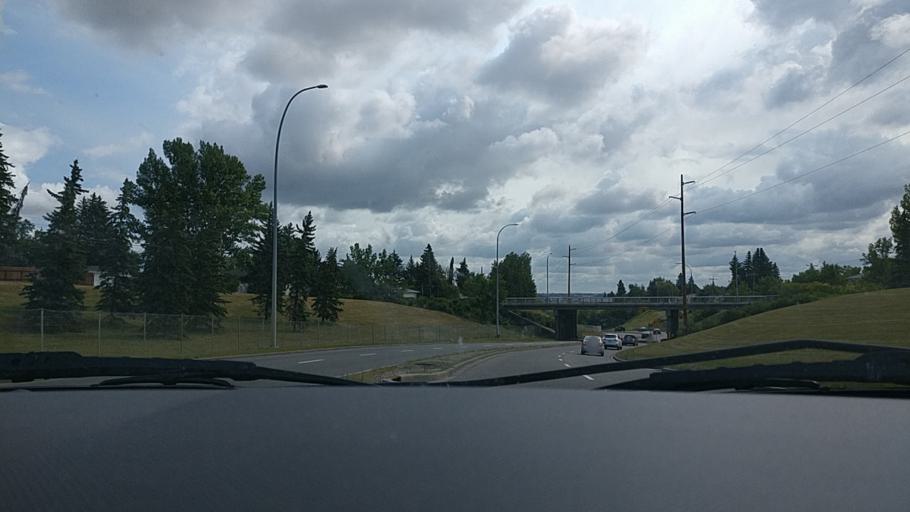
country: CA
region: Alberta
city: Calgary
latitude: 51.0964
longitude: -114.0799
